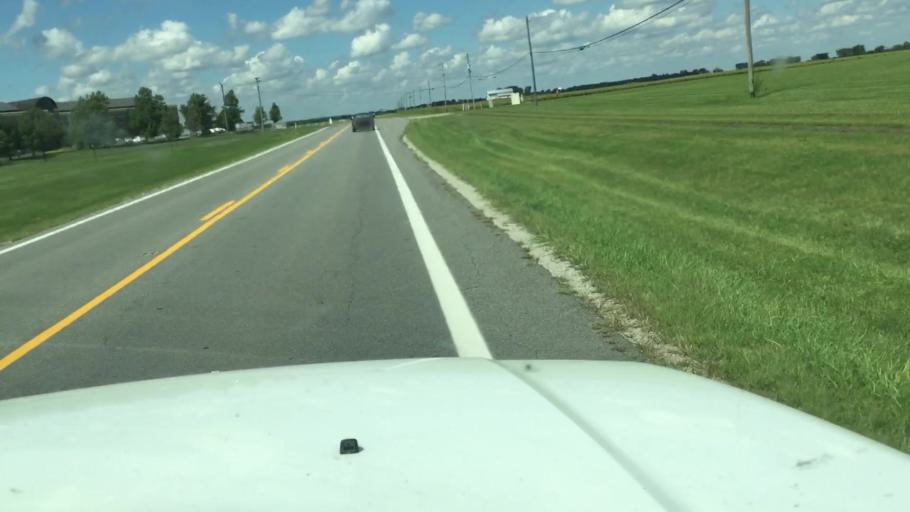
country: US
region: Ohio
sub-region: Madison County
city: London
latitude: 39.9108
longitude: -83.4749
